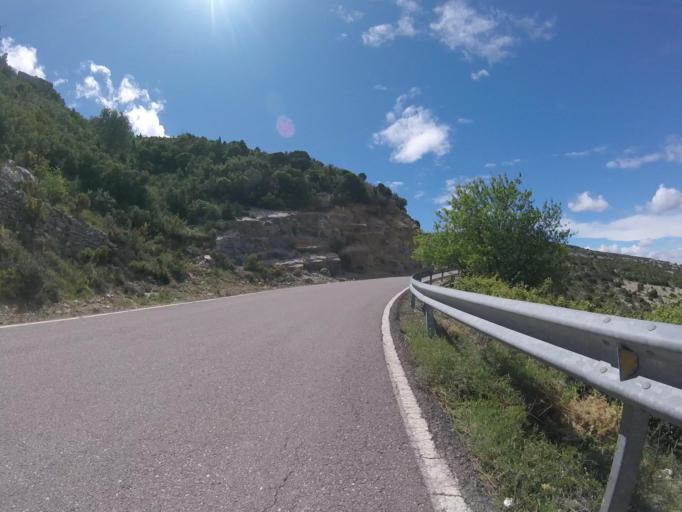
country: ES
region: Valencia
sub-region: Provincia de Castello
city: Sierra-Engarceran
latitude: 40.2823
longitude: -0.0314
